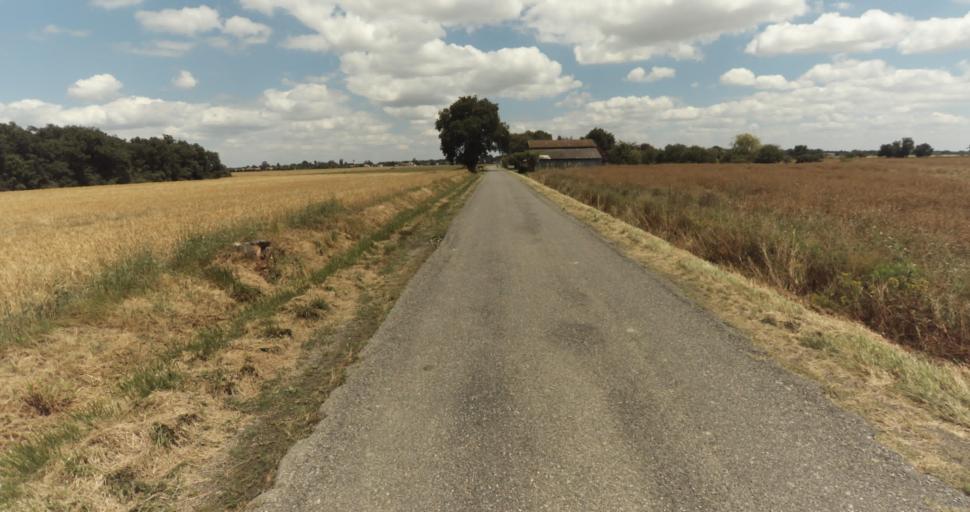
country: FR
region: Midi-Pyrenees
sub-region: Departement de la Haute-Garonne
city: Fontenilles
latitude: 43.5399
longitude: 1.1717
